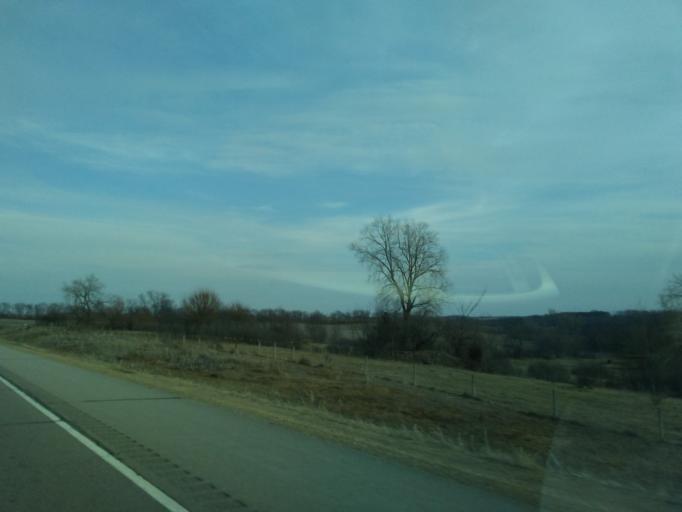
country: US
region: Wisconsin
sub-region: Iowa County
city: Dodgeville
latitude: 42.9672
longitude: -90.0903
